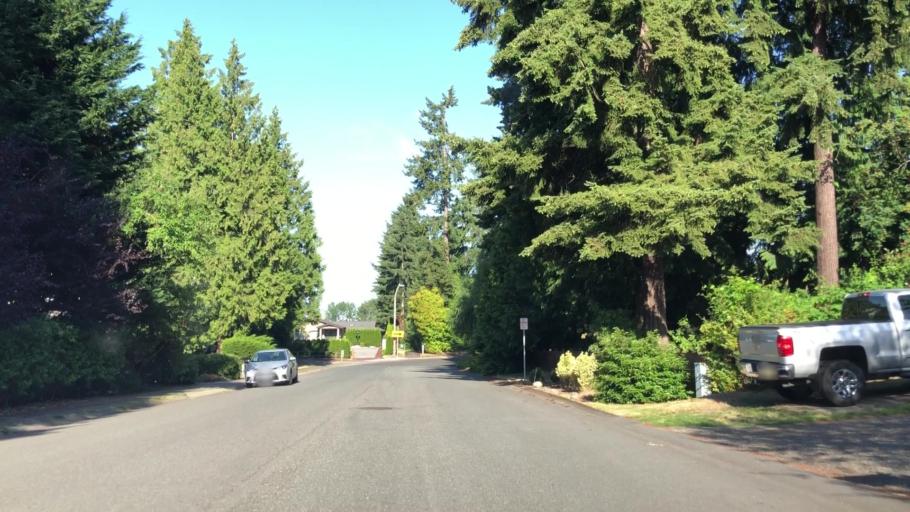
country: US
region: Washington
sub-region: King County
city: Eastgate
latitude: 47.6189
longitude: -122.1472
